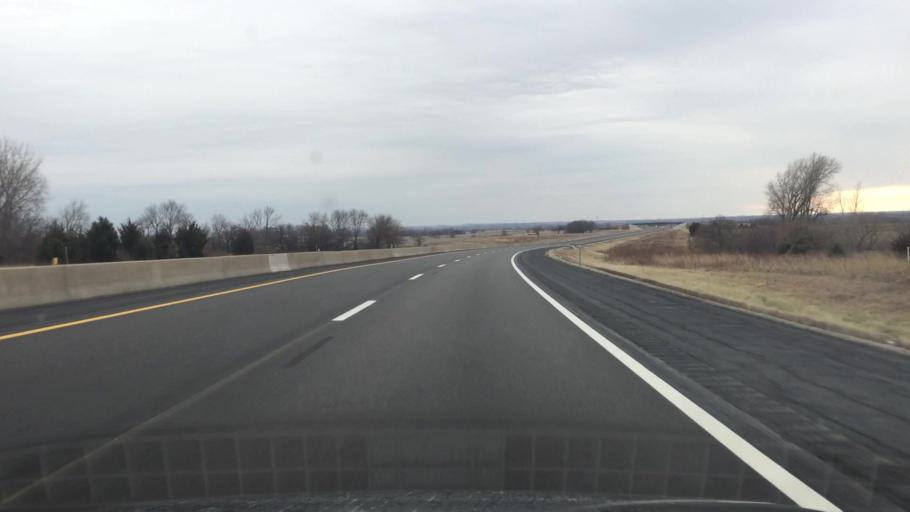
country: US
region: Kansas
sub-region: Shawnee County
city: Auburn
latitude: 38.8041
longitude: -95.9017
